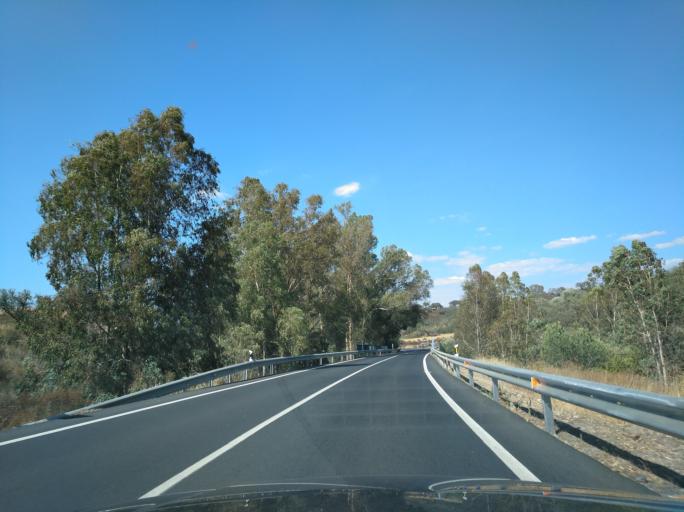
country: ES
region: Andalusia
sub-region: Provincia de Huelva
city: Alosno
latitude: 37.5277
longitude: -7.1340
